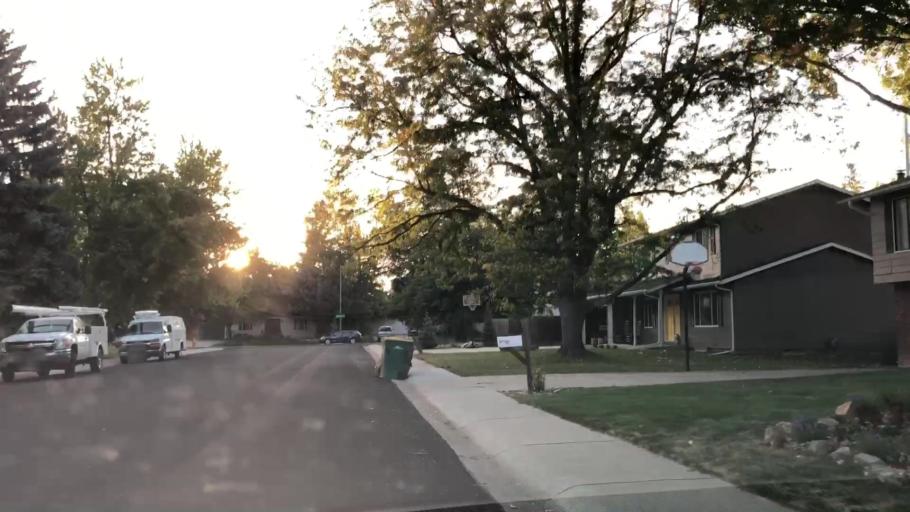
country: US
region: Colorado
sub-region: Larimer County
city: Fort Collins
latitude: 40.5520
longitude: -105.0508
